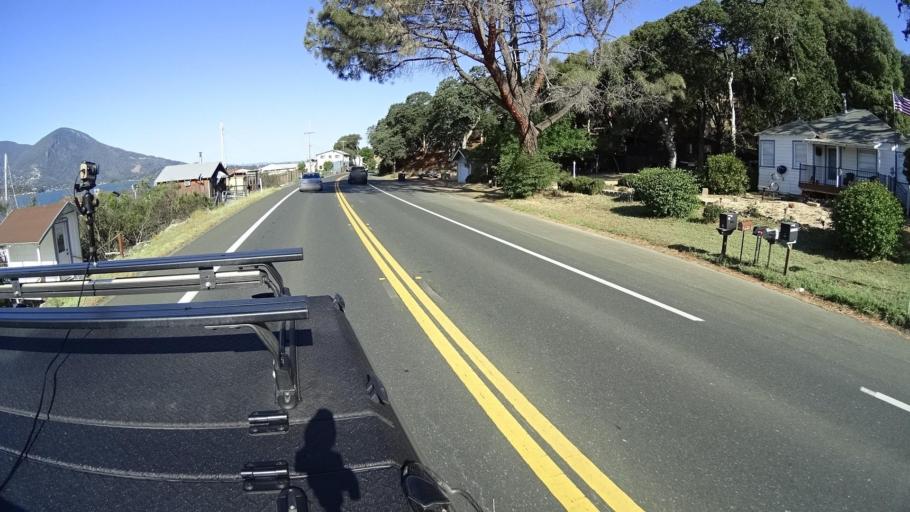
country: US
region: California
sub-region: Lake County
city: Clearlake Oaks
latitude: 39.0206
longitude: -122.7083
